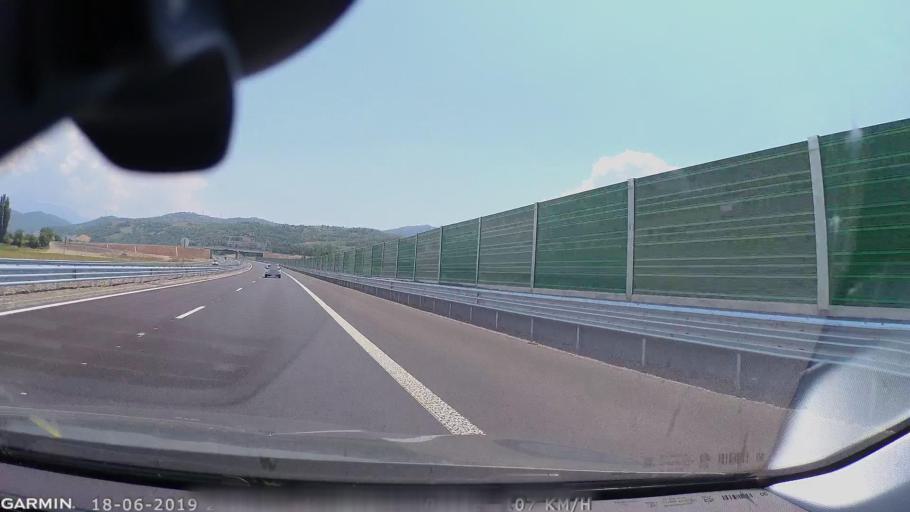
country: BG
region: Blagoevgrad
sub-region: Obshtina Blagoevgrad
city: Blagoevgrad
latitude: 41.9892
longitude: 23.0552
